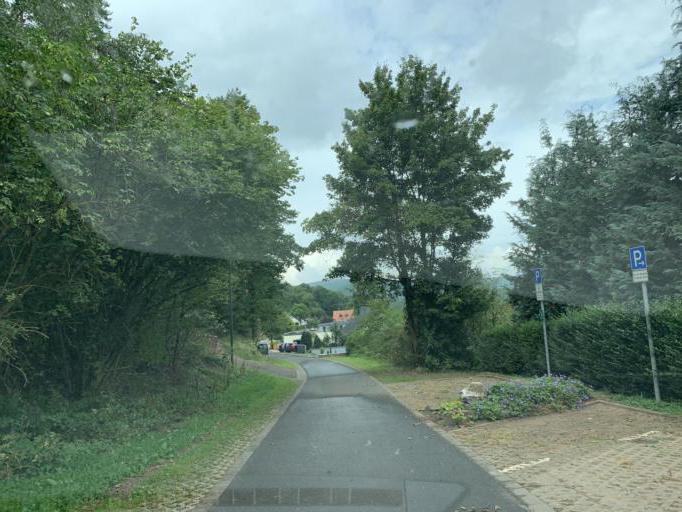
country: DE
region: North Rhine-Westphalia
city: Heimbach
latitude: 50.6495
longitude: 6.4981
